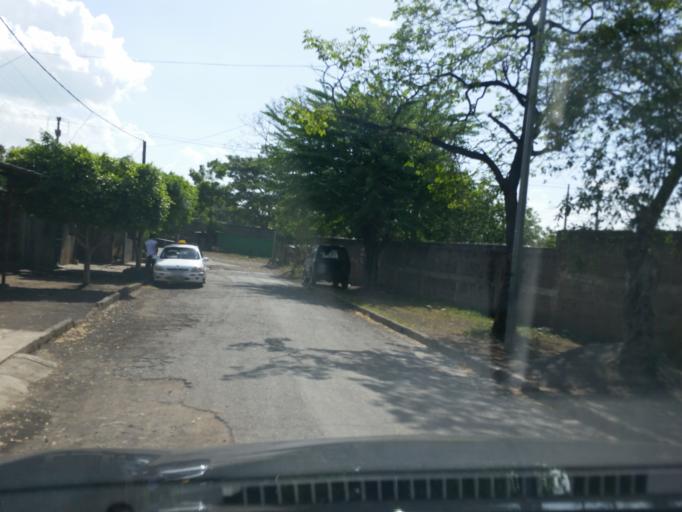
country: NI
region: Managua
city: Managua
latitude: 12.1545
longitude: -86.2358
